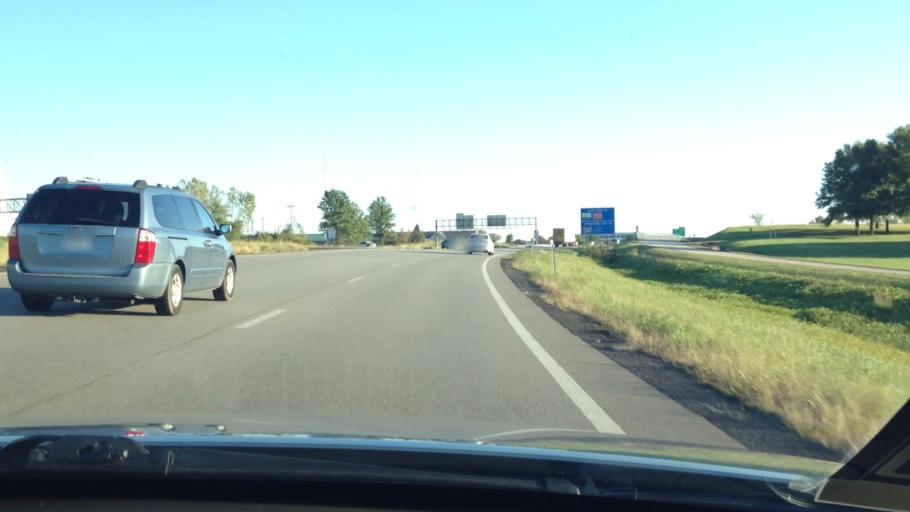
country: US
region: Missouri
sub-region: Platte County
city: Weatherby Lake
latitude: 39.3090
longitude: -94.6877
